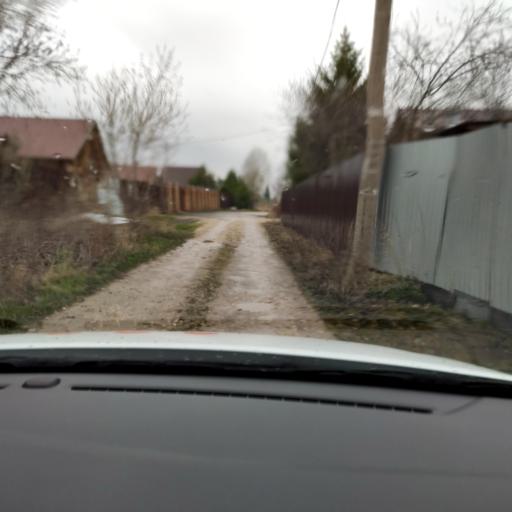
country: RU
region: Tatarstan
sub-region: Gorod Kazan'
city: Kazan
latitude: 55.6879
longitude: 49.0673
